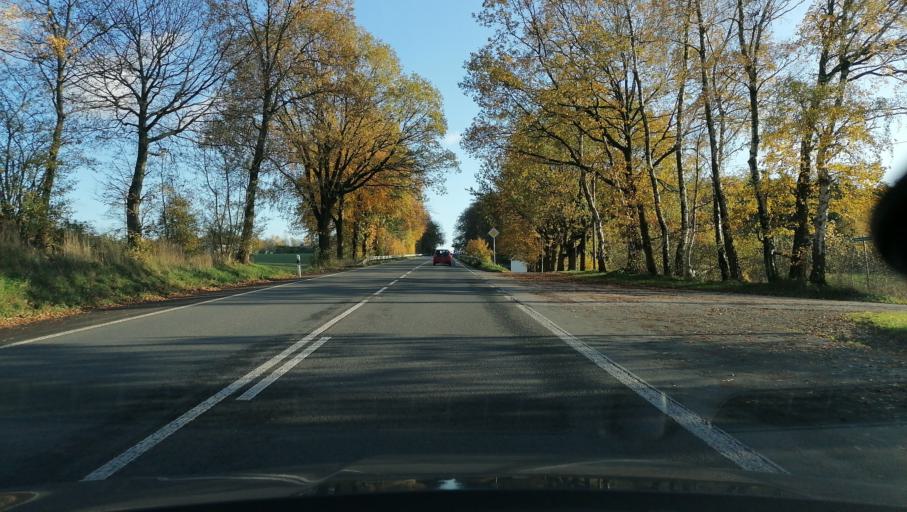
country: DE
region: North Rhine-Westphalia
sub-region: Regierungsbezirk Arnsberg
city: Schwelm
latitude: 51.2707
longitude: 7.3200
